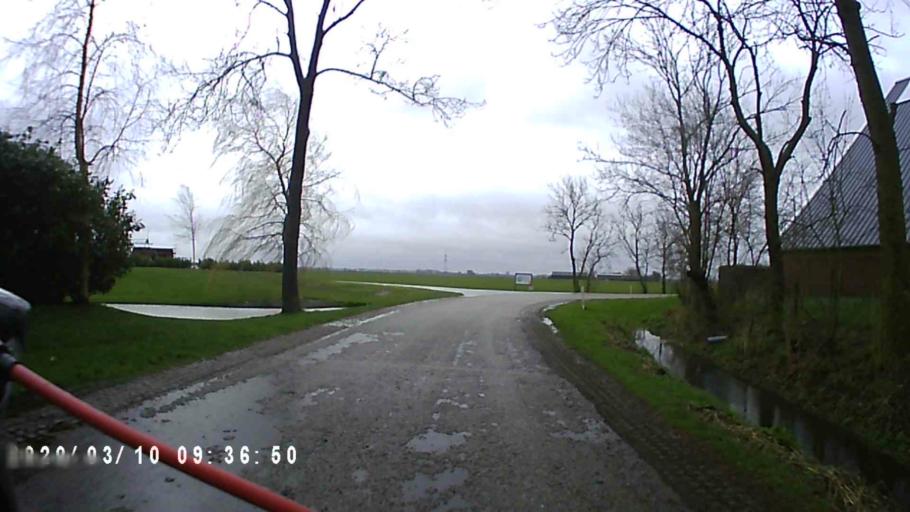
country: NL
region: Groningen
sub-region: Gemeente Winsum
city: Winsum
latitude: 53.2998
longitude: 6.4919
